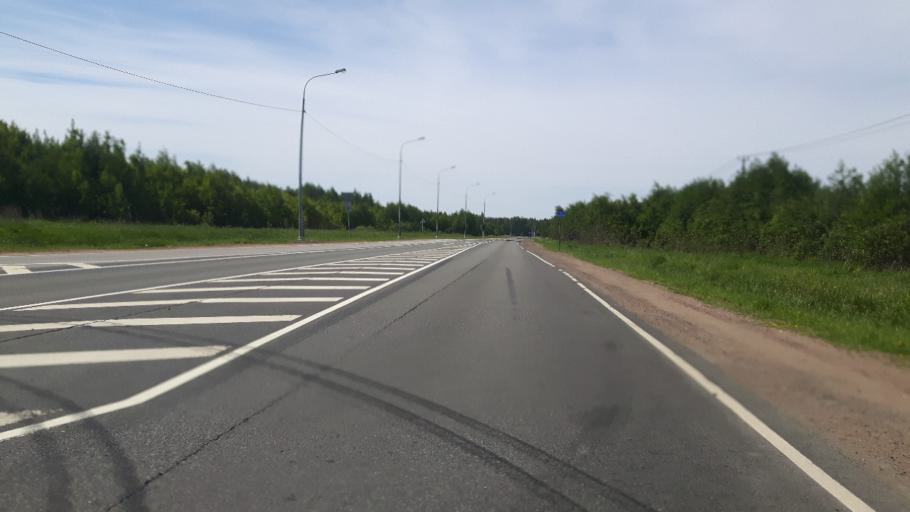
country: RU
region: Leningrad
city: Ust'-Luga
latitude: 59.6543
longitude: 28.3797
